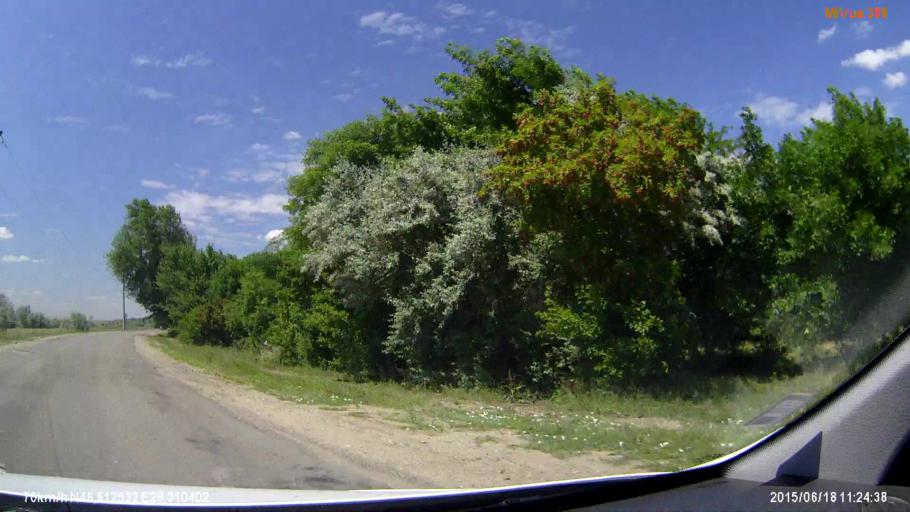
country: MD
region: Causeni
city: Causeni
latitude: 46.6125
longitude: 29.3109
